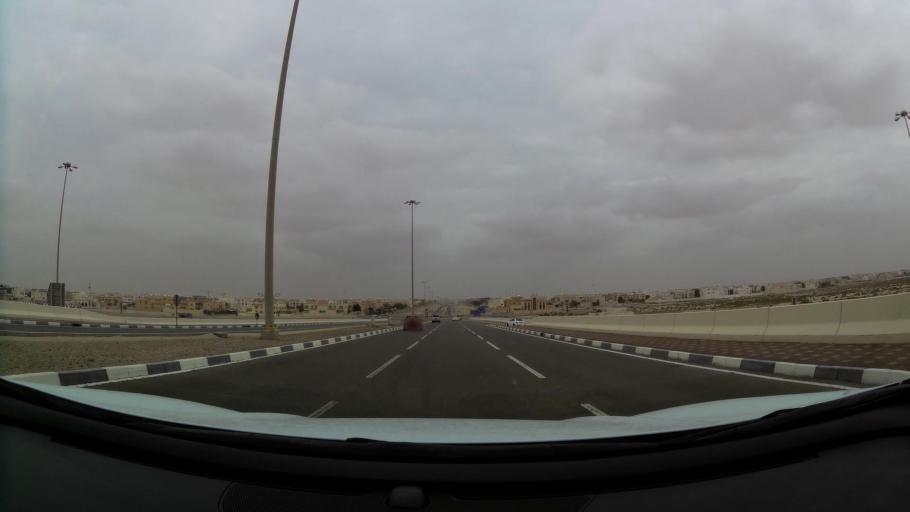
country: AE
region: Abu Dhabi
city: Abu Dhabi
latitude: 24.3701
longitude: 54.6533
